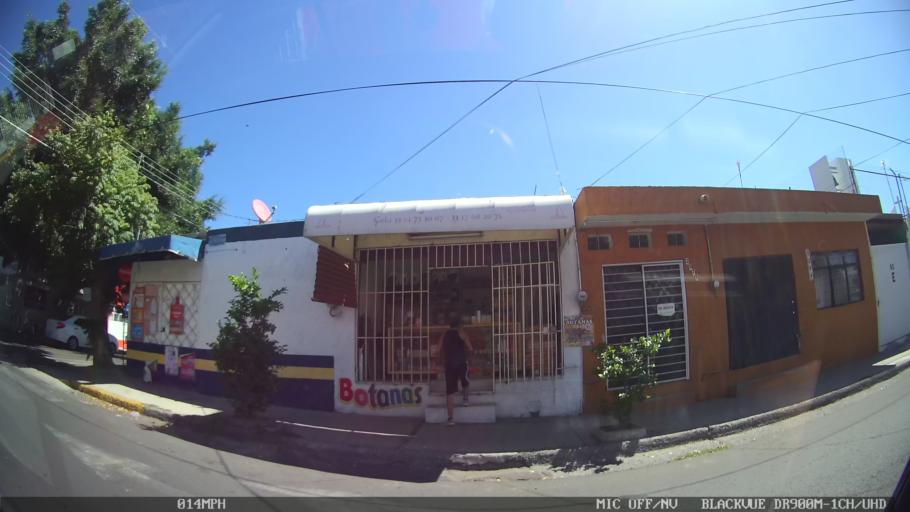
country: MX
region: Jalisco
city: Tlaquepaque
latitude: 20.6946
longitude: -103.2869
